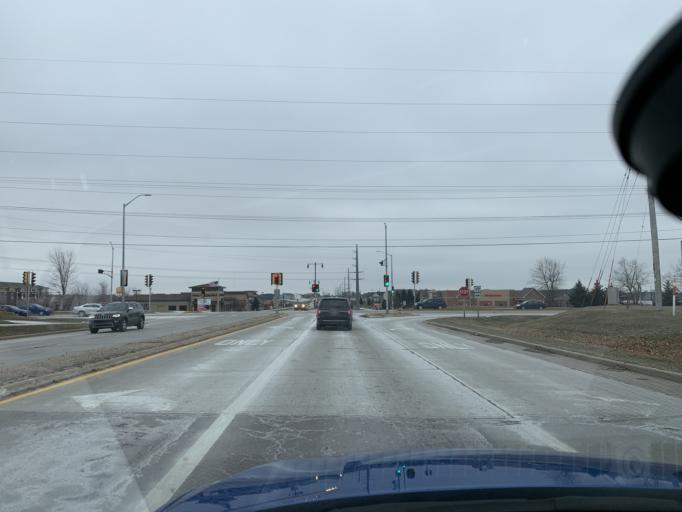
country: US
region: Wisconsin
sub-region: Dane County
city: Sun Prairie
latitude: 43.1876
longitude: -89.2645
